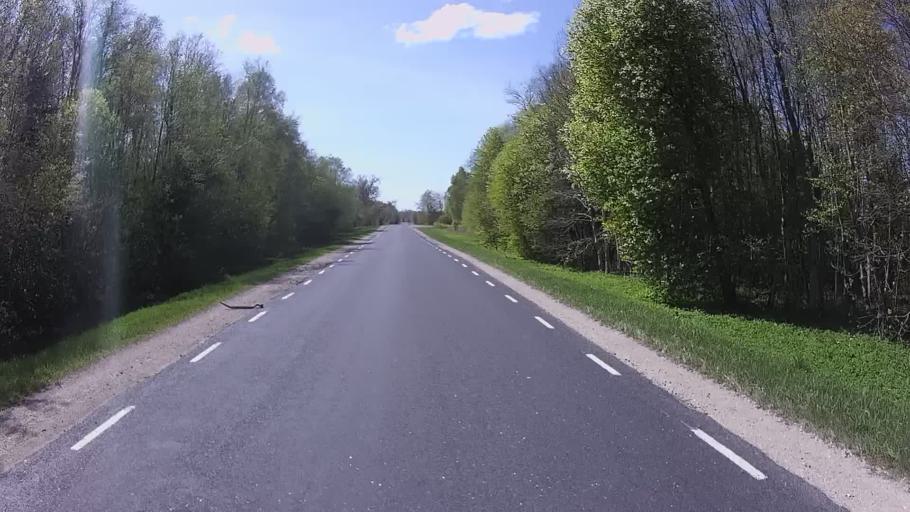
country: EE
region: Laeaene
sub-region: Ridala Parish
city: Uuemoisa
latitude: 59.0174
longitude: 23.7944
